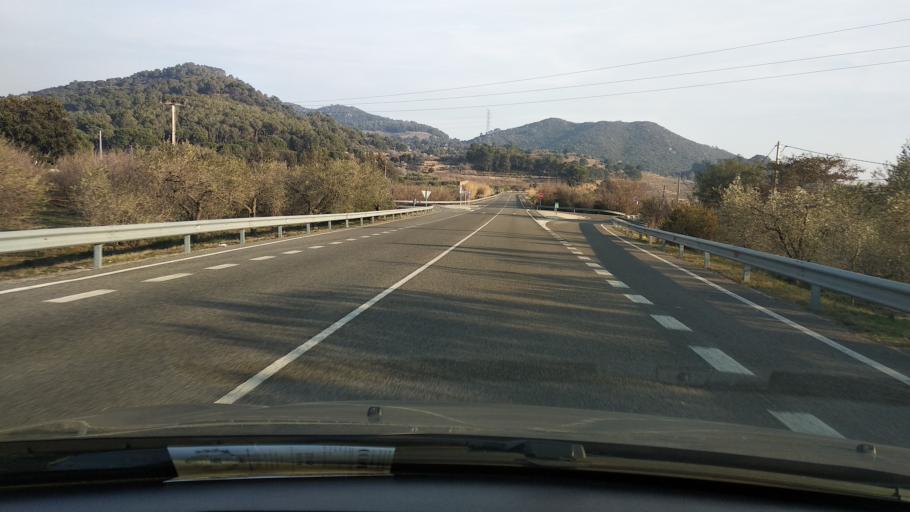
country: ES
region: Catalonia
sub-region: Provincia de Tarragona
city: Alforja
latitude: 41.2051
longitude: 0.9917
